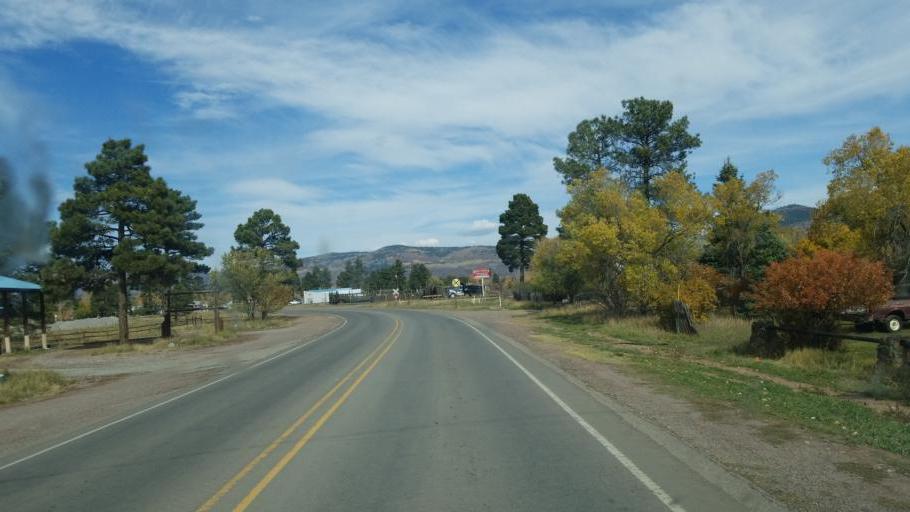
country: US
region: New Mexico
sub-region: Rio Arriba County
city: Chama
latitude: 36.8949
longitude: -106.5817
